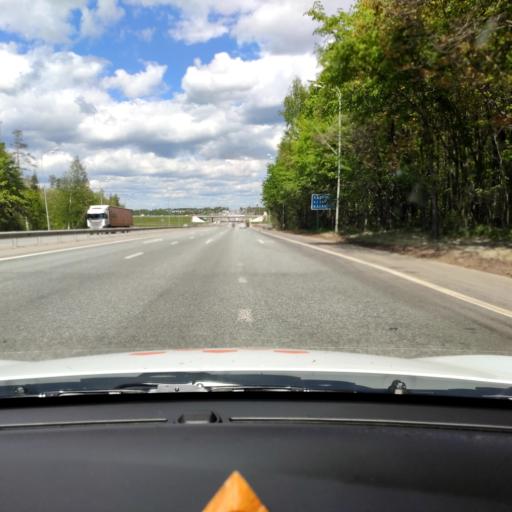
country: RU
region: Tatarstan
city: Osinovo
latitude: 55.8522
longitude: 48.8539
